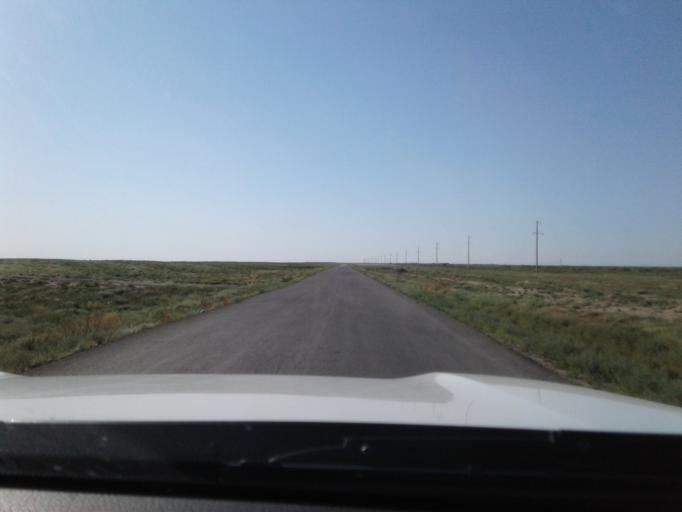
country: IR
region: Razavi Khorasan
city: Kalat-e Naderi
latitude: 37.1465
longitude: 60.0644
